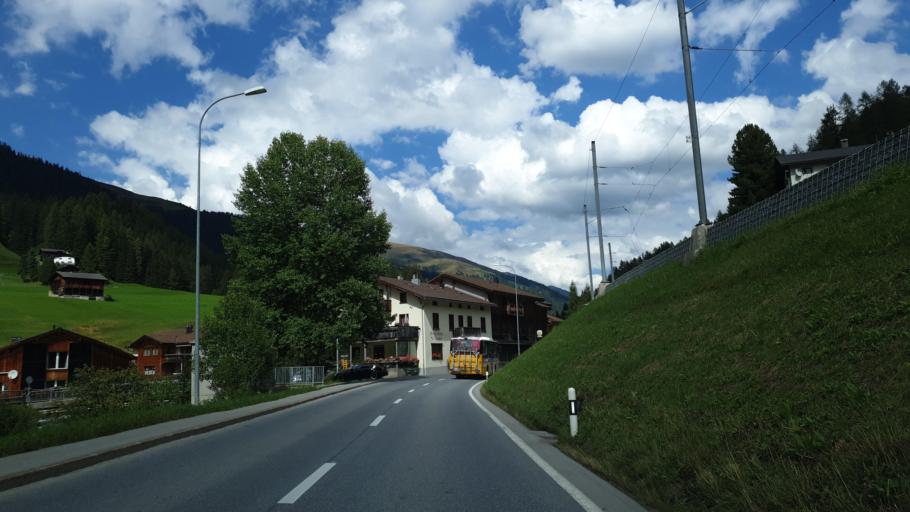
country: CH
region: Grisons
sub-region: Praettigau/Davos District
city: Davos
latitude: 46.7410
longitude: 9.7780
